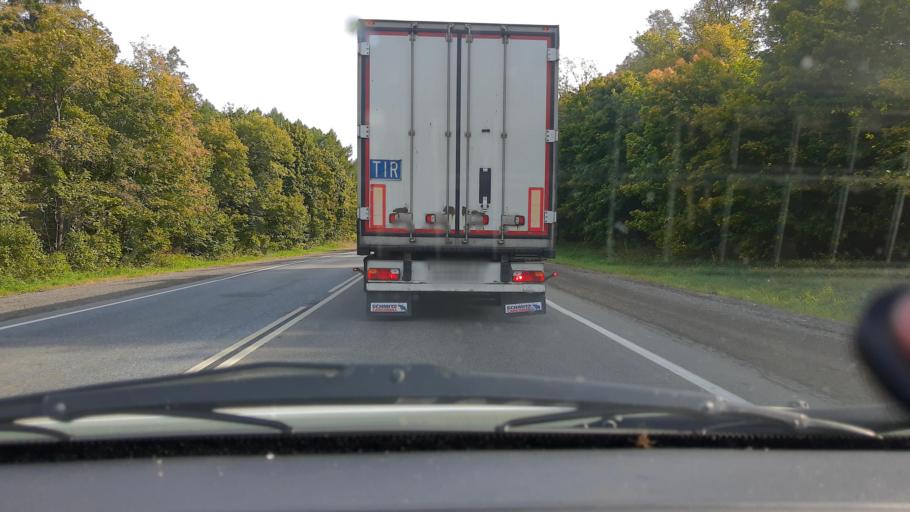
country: RU
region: Bashkortostan
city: Iglino
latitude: 54.7698
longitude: 56.4474
